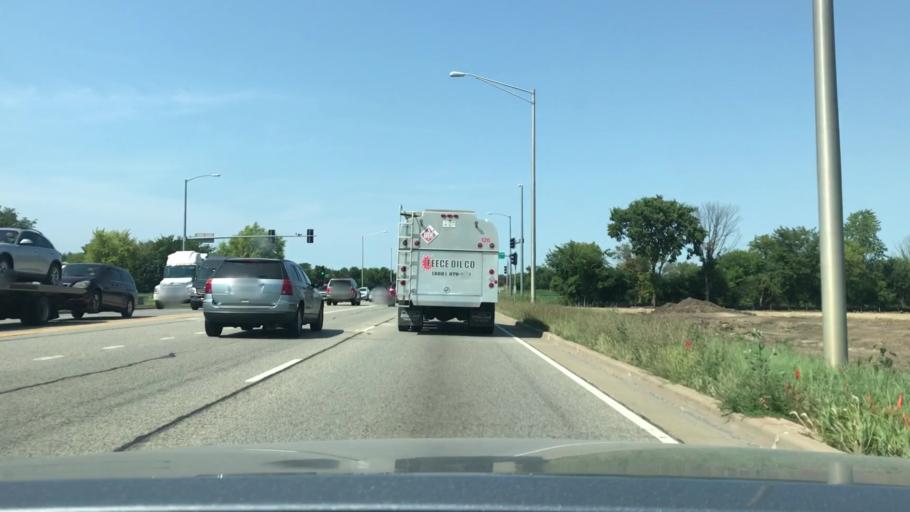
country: US
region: Illinois
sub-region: Kane County
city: Batavia
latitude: 41.8235
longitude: -88.2798
